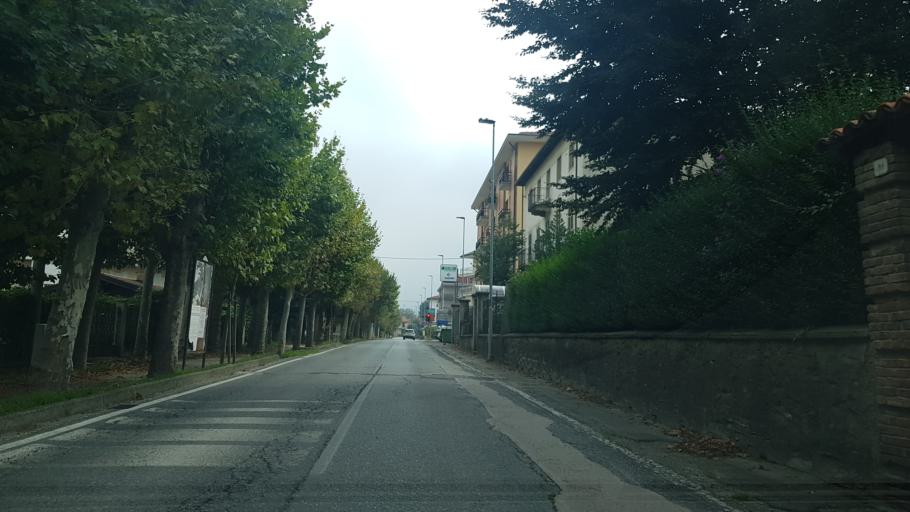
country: IT
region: Piedmont
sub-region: Provincia di Cuneo
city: Peveragno
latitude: 44.3291
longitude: 7.6166
